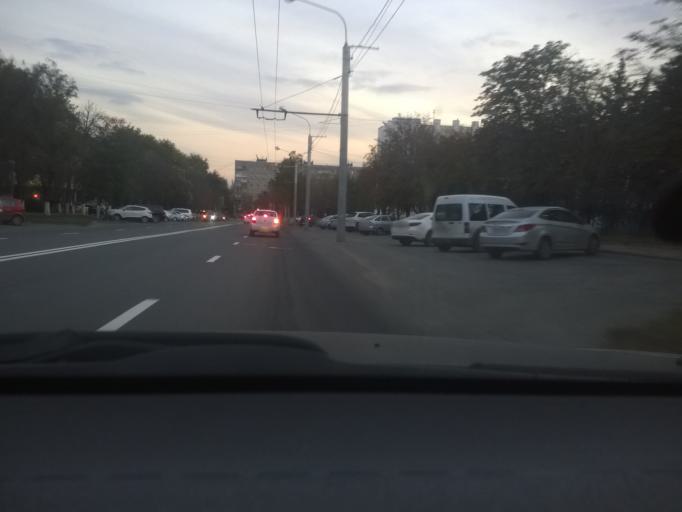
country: RU
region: Rostov
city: Rostov-na-Donu
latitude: 47.2101
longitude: 39.6350
